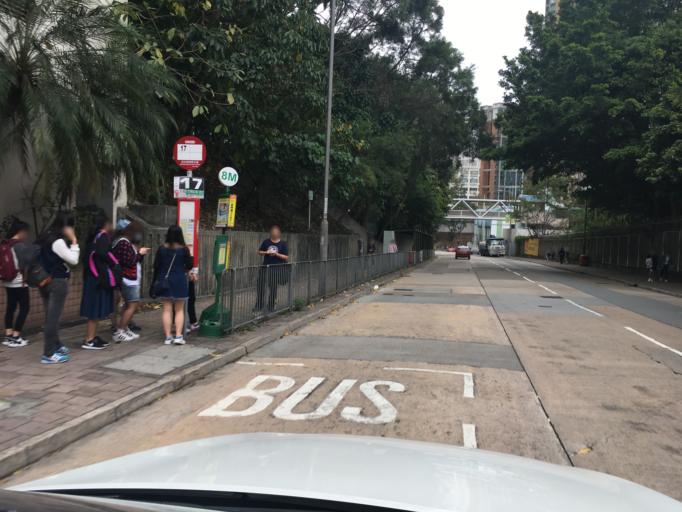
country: HK
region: Kowloon City
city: Kowloon
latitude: 22.3184
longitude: 114.1807
